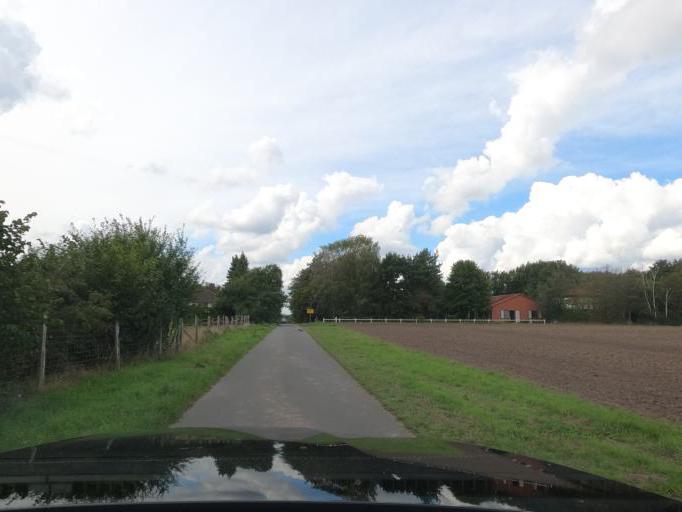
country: DE
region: Lower Saxony
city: Isernhagen Farster Bauerschaft
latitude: 52.5166
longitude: 9.9253
